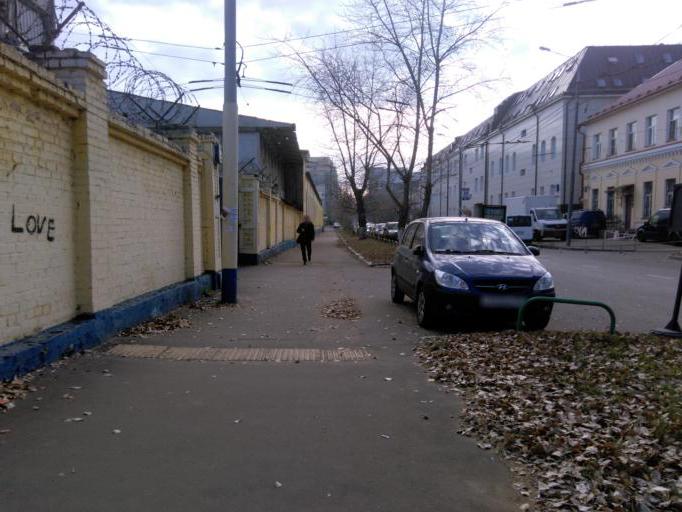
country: RU
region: Moscow
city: Mar'ina Roshcha
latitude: 55.8035
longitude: 37.5847
